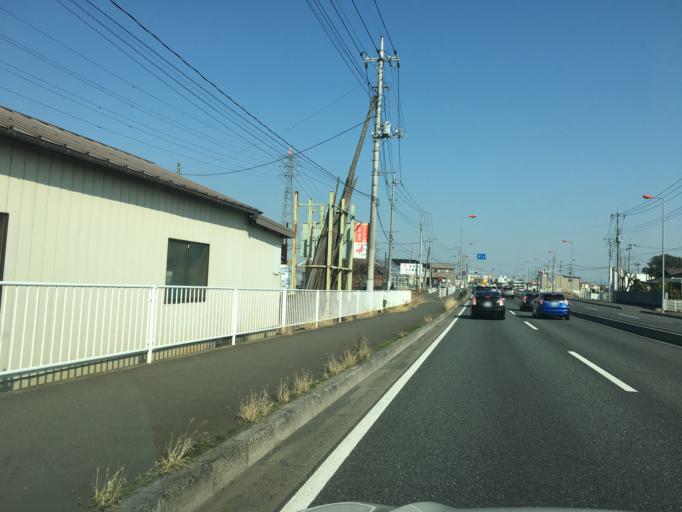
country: JP
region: Saitama
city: Kawagoe
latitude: 35.9192
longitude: 139.5103
